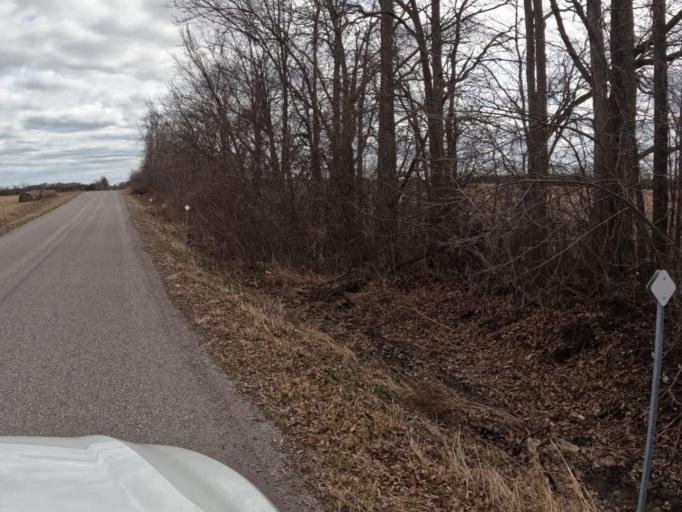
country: CA
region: Ontario
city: Norfolk County
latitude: 42.8631
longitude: -80.1749
